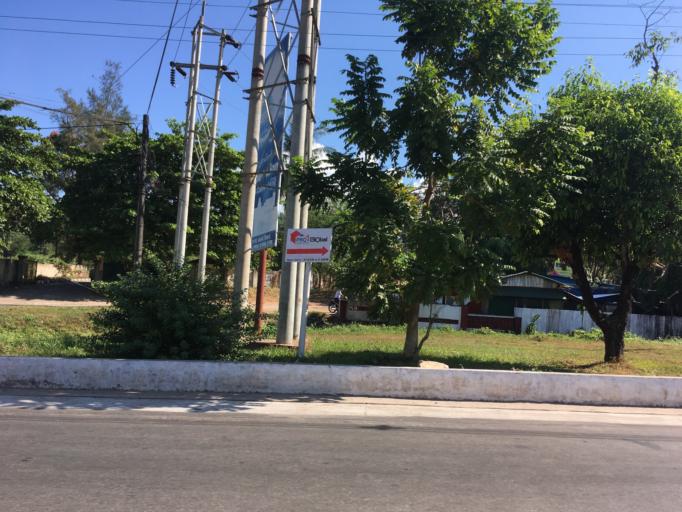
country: MM
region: Mon
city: Mawlamyine
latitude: 16.4644
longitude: 97.6280
